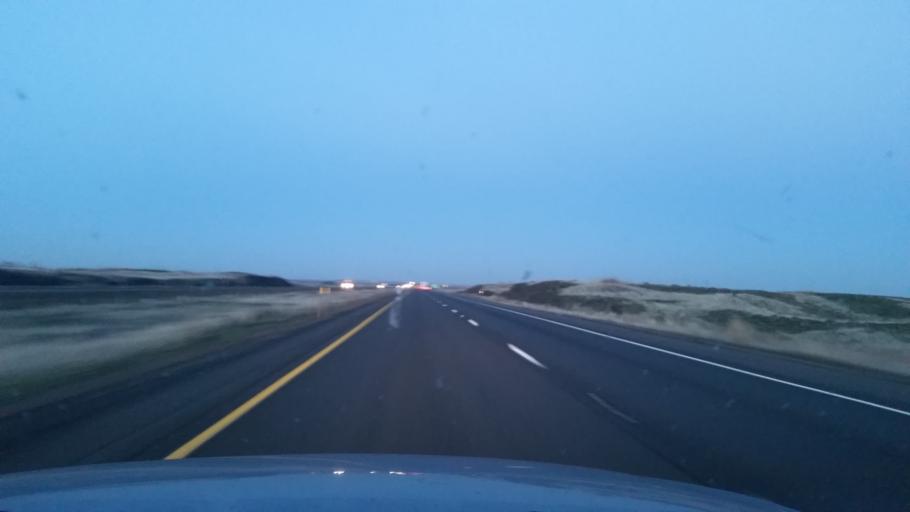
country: US
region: Washington
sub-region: Adams County
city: Ritzville
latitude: 47.1446
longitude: -118.3252
